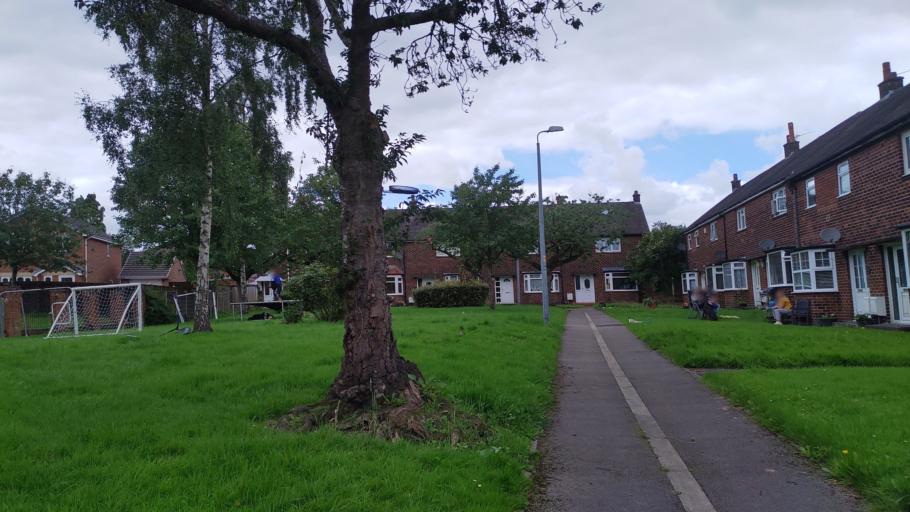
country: GB
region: England
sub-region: Lancashire
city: Chorley
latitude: 53.6417
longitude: -2.6355
